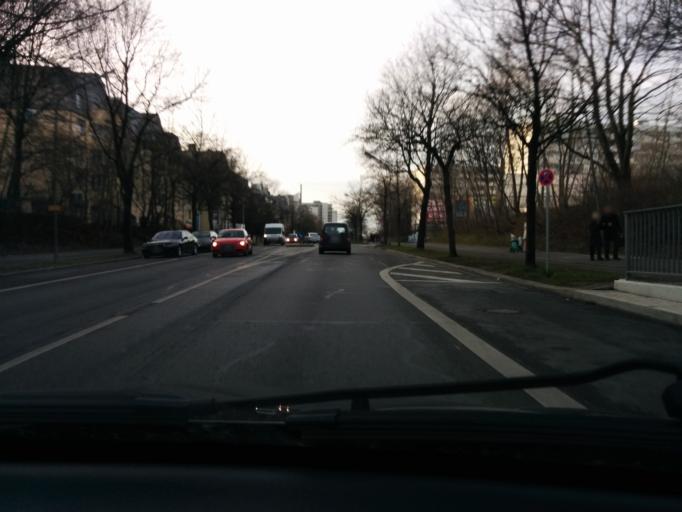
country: DE
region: Bavaria
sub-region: Upper Bavaria
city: Pasing
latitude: 48.1491
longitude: 11.4430
